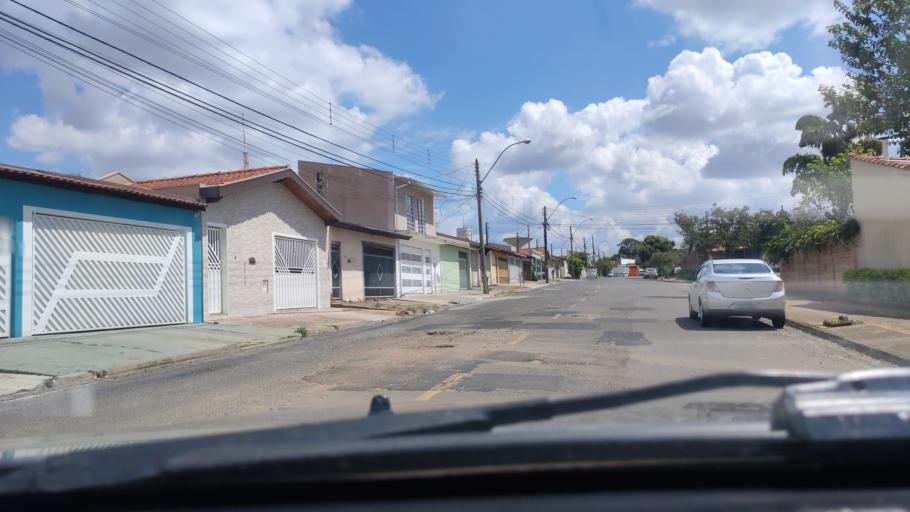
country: BR
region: Sao Paulo
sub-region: Sao Carlos
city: Sao Carlos
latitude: -22.0097
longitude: -47.8665
